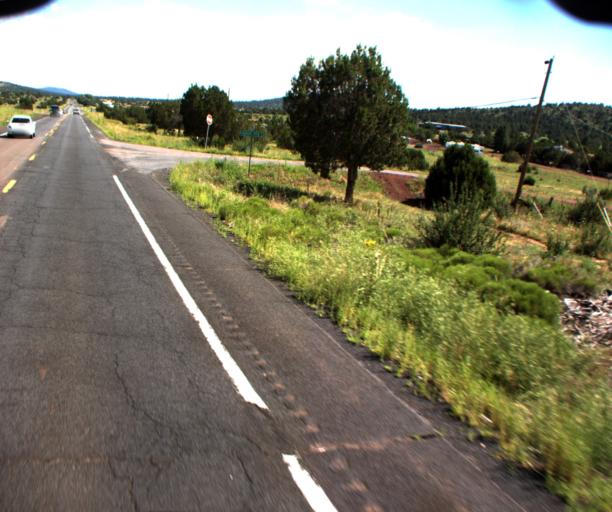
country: US
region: Arizona
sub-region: Coconino County
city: Williams
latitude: 35.3315
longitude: -112.1575
